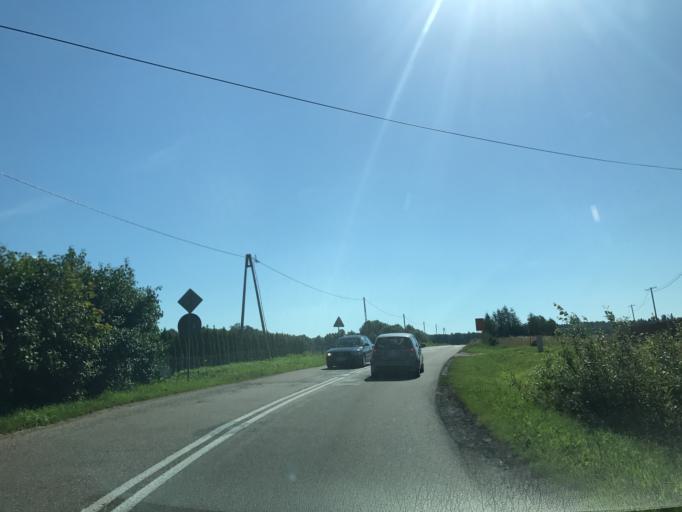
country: PL
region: Pomeranian Voivodeship
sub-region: Powiat bytowski
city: Czarna Dabrowka
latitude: 54.3549
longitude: 17.5697
